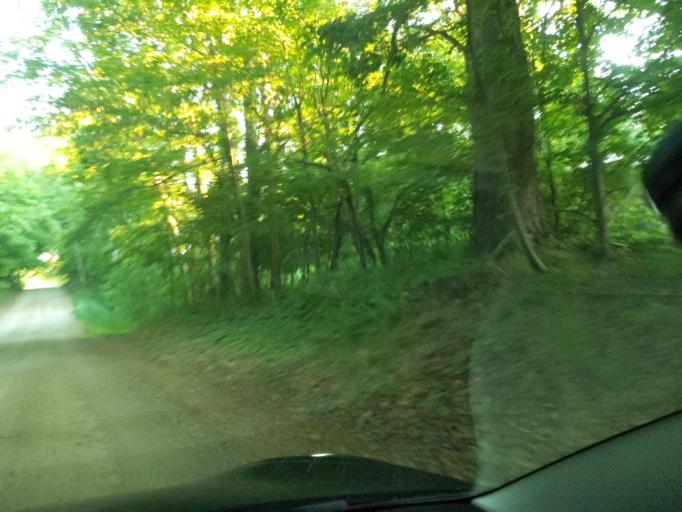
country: US
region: Michigan
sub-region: Barry County
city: Nashville
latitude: 42.5337
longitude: -85.1133
